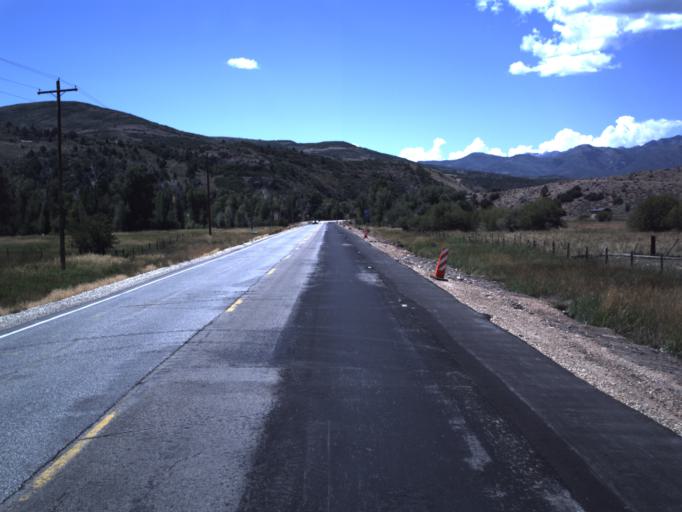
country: US
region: Utah
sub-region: Summit County
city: Francis
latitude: 40.6039
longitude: -111.3221
